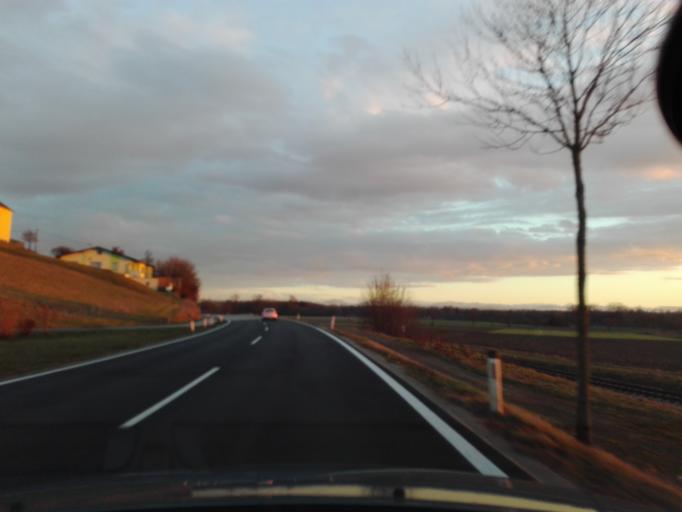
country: AT
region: Upper Austria
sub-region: Politischer Bezirk Perg
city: Perg
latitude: 48.2245
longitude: 14.7040
